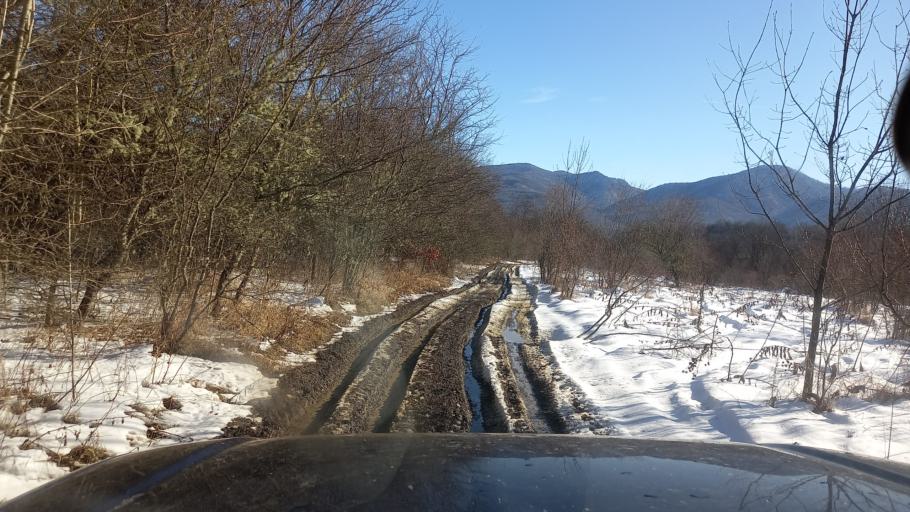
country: RU
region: Adygeya
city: Kamennomostskiy
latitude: 44.2094
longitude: 40.1451
